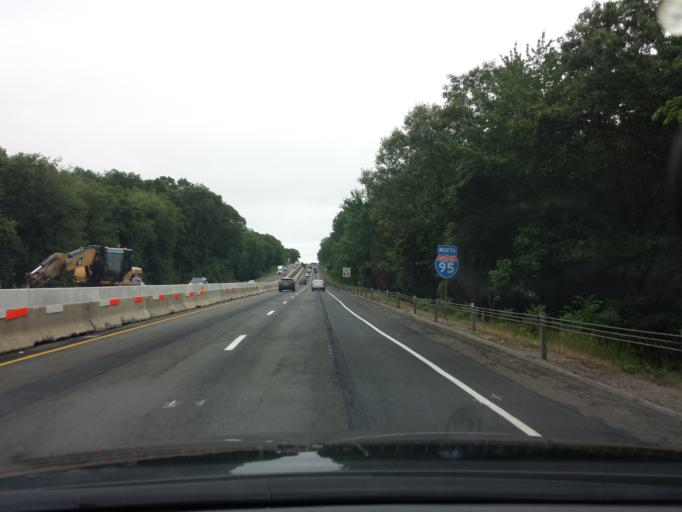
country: US
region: Connecticut
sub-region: Middlesex County
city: Old Saybrook Center
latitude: 41.3225
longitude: -72.3219
